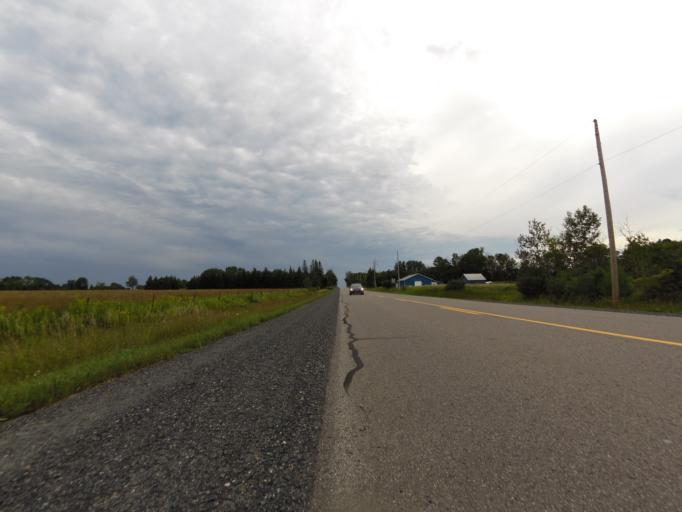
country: CA
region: Ontario
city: Carleton Place
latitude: 45.1009
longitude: -76.3909
